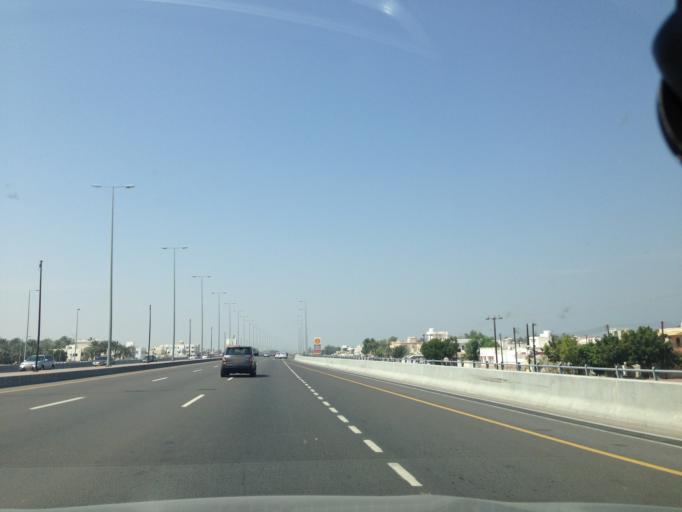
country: OM
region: Muhafazat Masqat
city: As Sib al Jadidah
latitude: 23.6676
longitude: 58.1553
